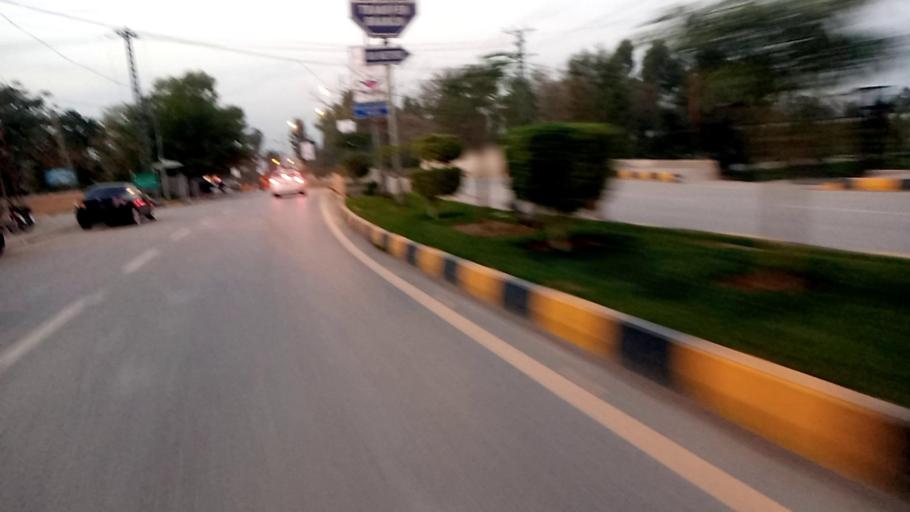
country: PK
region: Khyber Pakhtunkhwa
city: Peshawar
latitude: 34.0158
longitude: 71.5480
